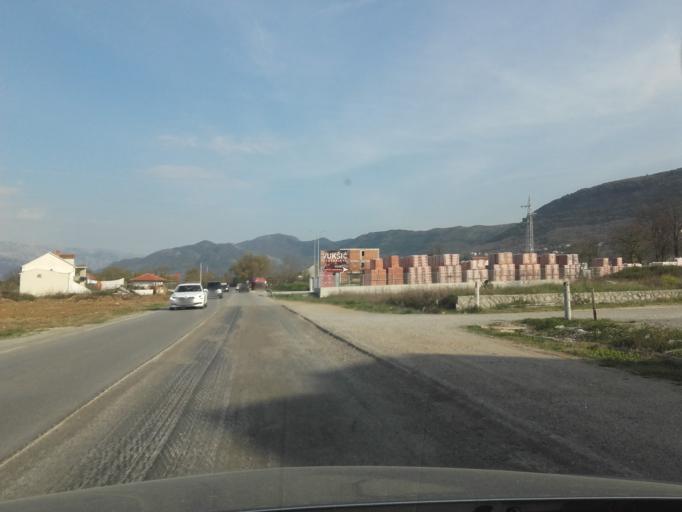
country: ME
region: Kotor
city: Kotor
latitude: 42.3719
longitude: 18.7534
